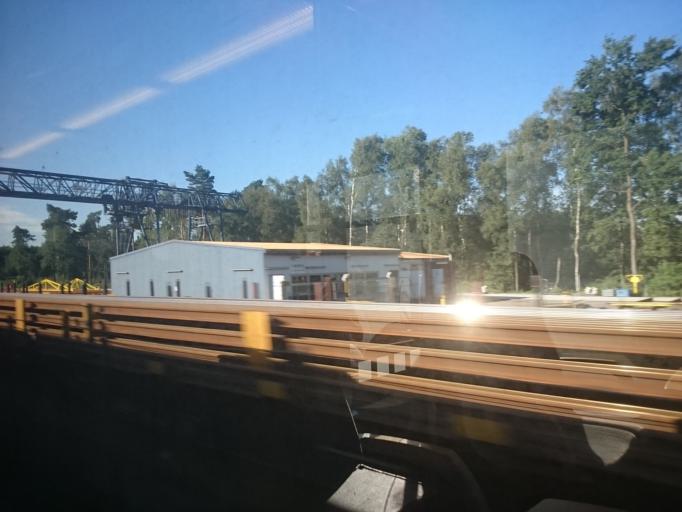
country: DE
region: North Rhine-Westphalia
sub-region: Regierungsbezirk Dusseldorf
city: Ratingen
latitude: 51.3600
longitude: 6.8175
